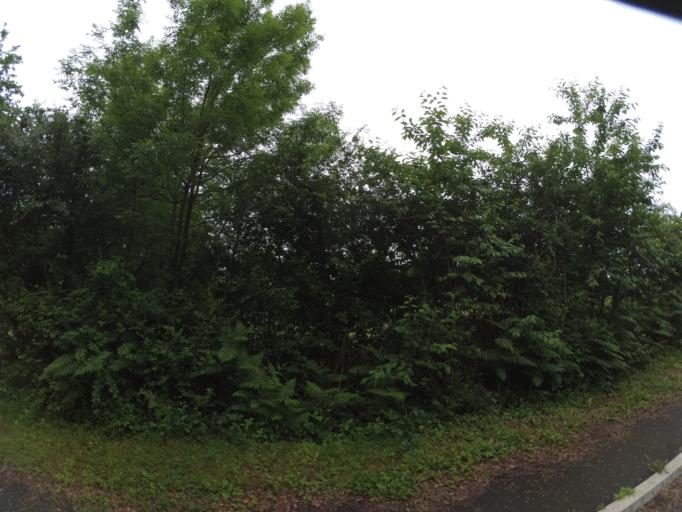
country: FR
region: Pays de la Loire
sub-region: Departement de la Vendee
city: La Roche-sur-Yon
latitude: 46.6380
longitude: -1.4320
